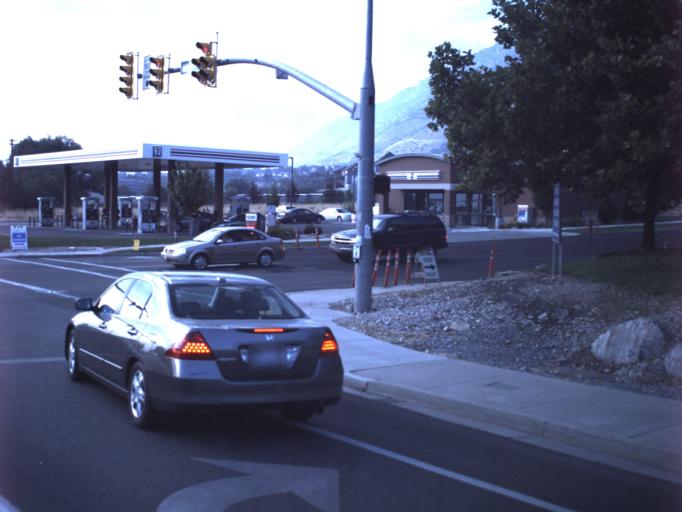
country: US
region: Utah
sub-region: Utah County
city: Provo
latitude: 40.2077
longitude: -111.6296
